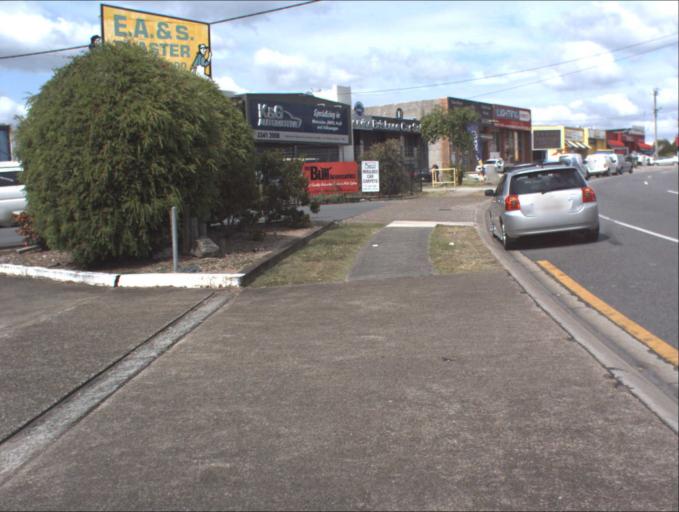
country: AU
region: Queensland
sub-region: Logan
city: Springwood
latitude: -27.6116
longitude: 153.1142
